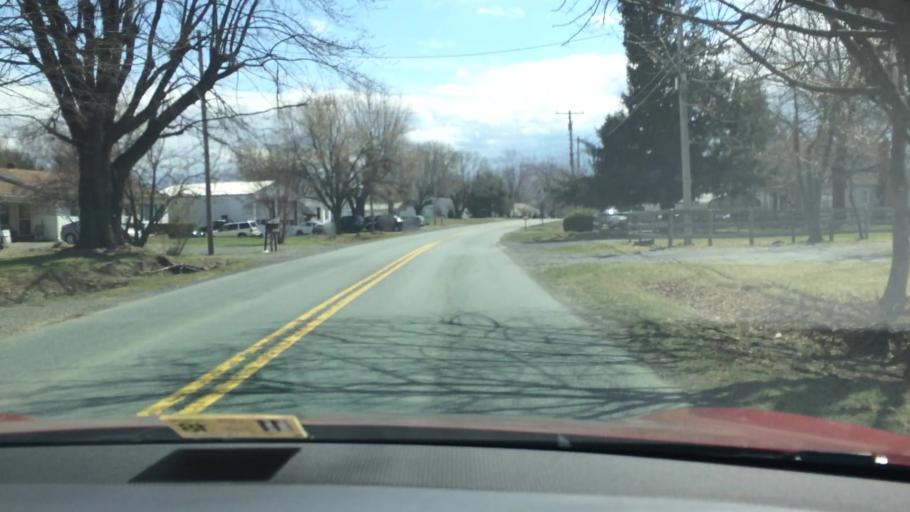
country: US
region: Virginia
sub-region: City of Winchester
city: Winchester
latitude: 39.2274
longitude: -78.1393
